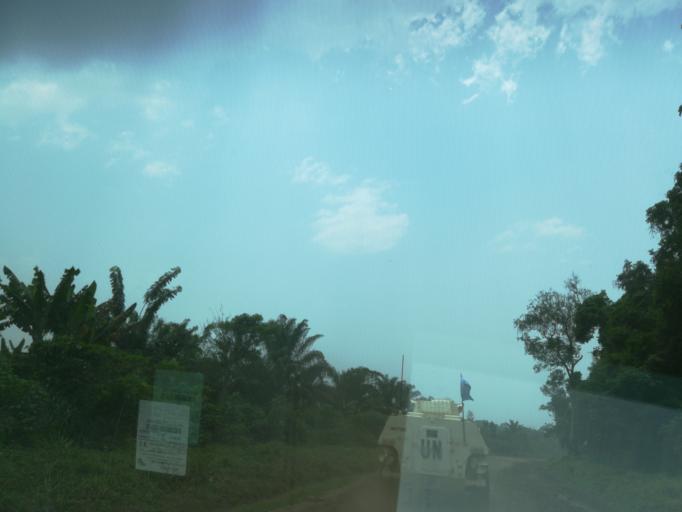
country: UG
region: Western Region
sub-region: Kasese District
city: Margherita
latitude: 0.2934
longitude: 29.6623
